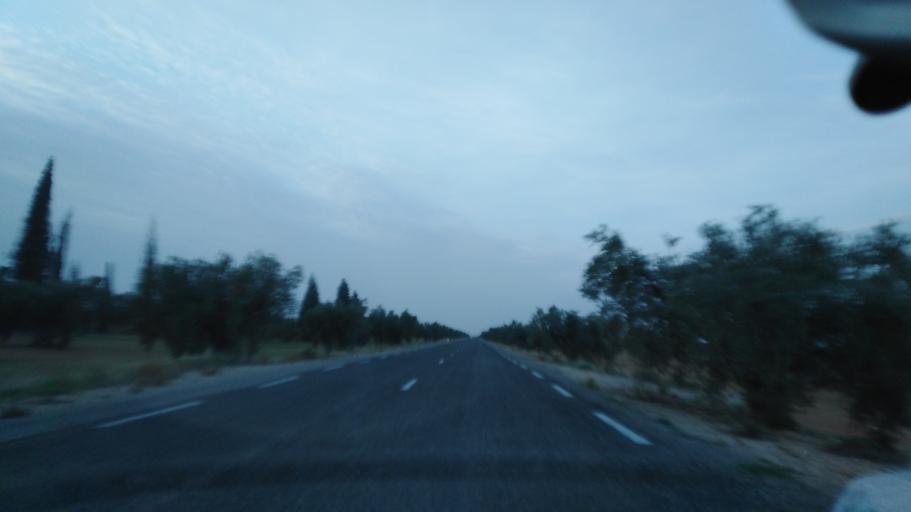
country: TN
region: Safaqis
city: Bi'r `Ali Bin Khalifah
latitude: 34.9129
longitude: 10.3876
